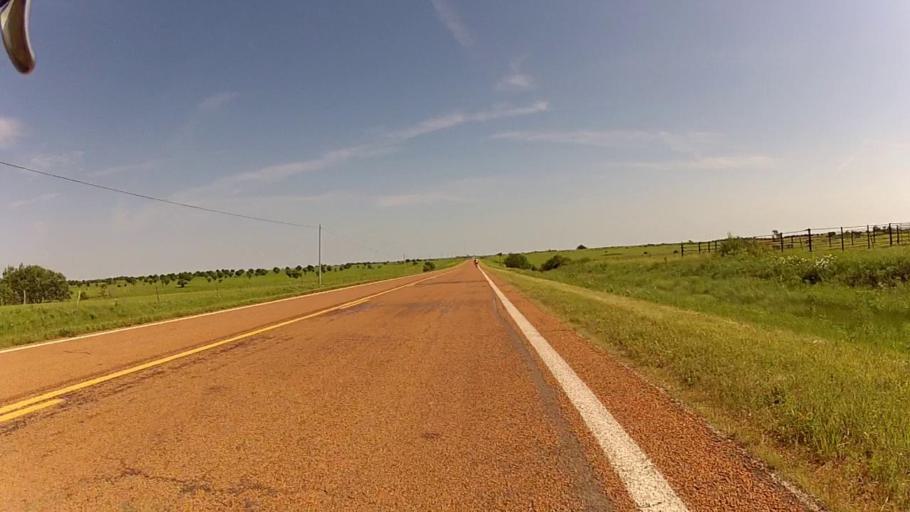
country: US
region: Kansas
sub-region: Cowley County
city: Winfield
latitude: 37.0874
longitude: -96.6435
